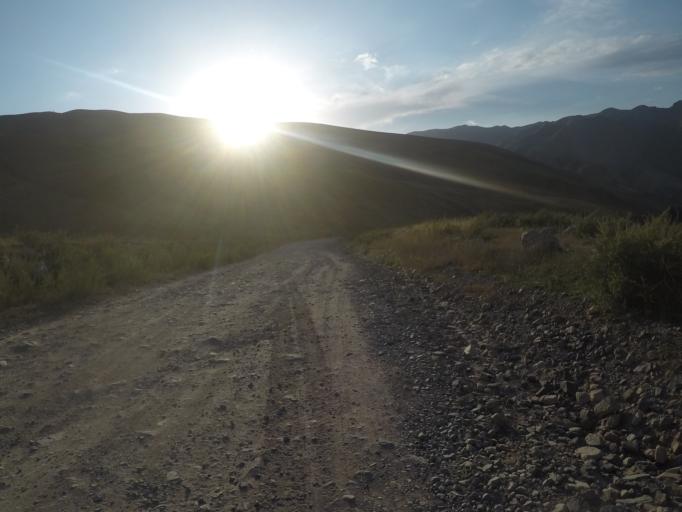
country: KG
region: Chuy
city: Bishkek
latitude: 42.6585
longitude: 74.6516
